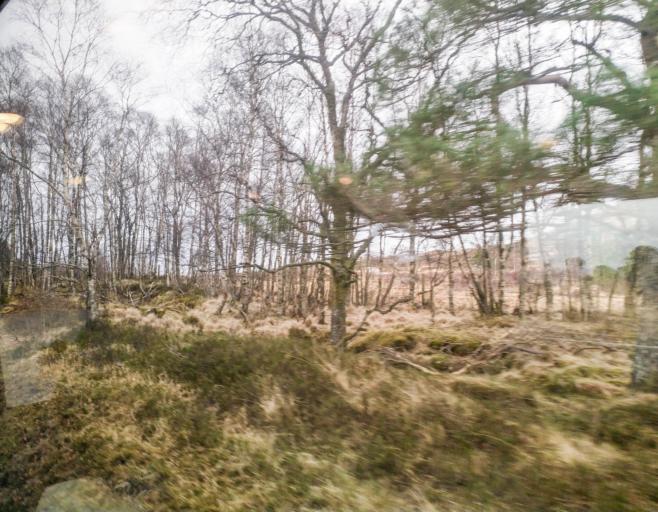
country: GB
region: Scotland
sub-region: Highland
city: Spean Bridge
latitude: 56.5817
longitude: -4.6751
